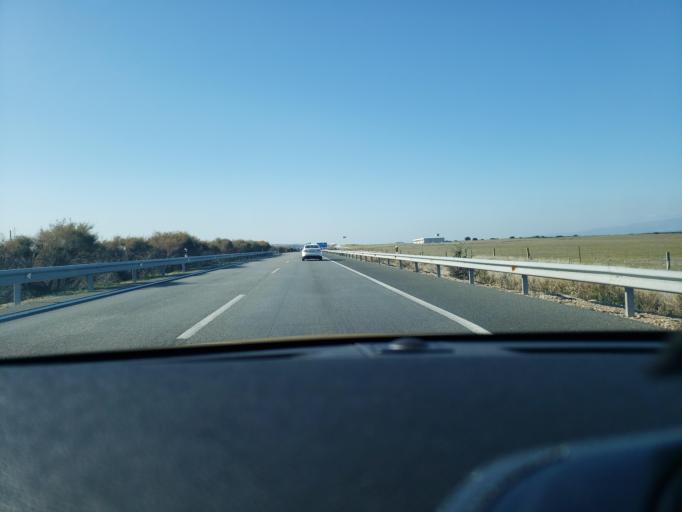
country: ES
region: Extremadura
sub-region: Provincia de Caceres
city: Peraleda de la Mata
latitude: 39.8917
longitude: -5.4102
